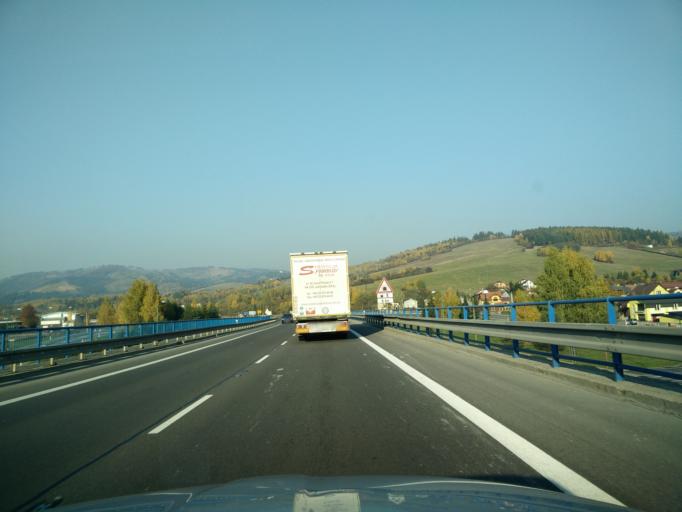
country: SK
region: Zilinsky
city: Cadca
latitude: 49.3999
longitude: 18.8412
